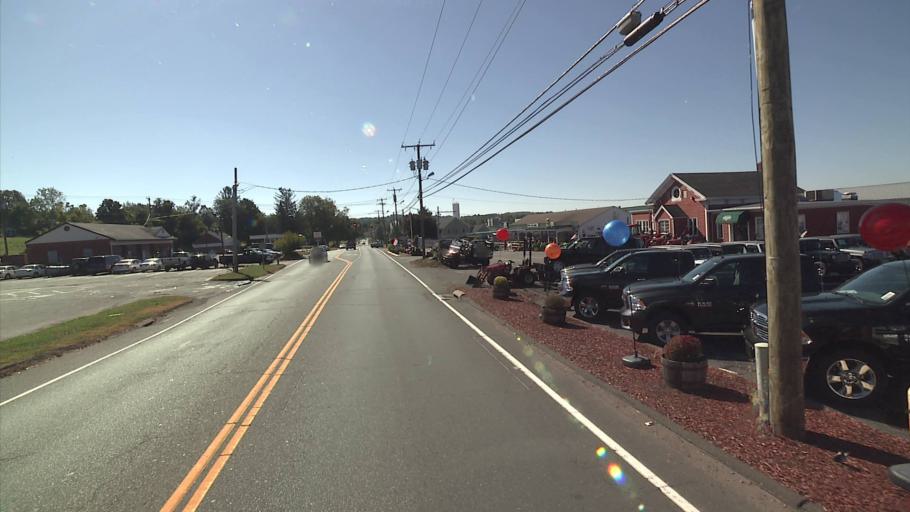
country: US
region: Connecticut
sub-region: Tolland County
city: Rockville
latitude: 41.8791
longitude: -72.4640
